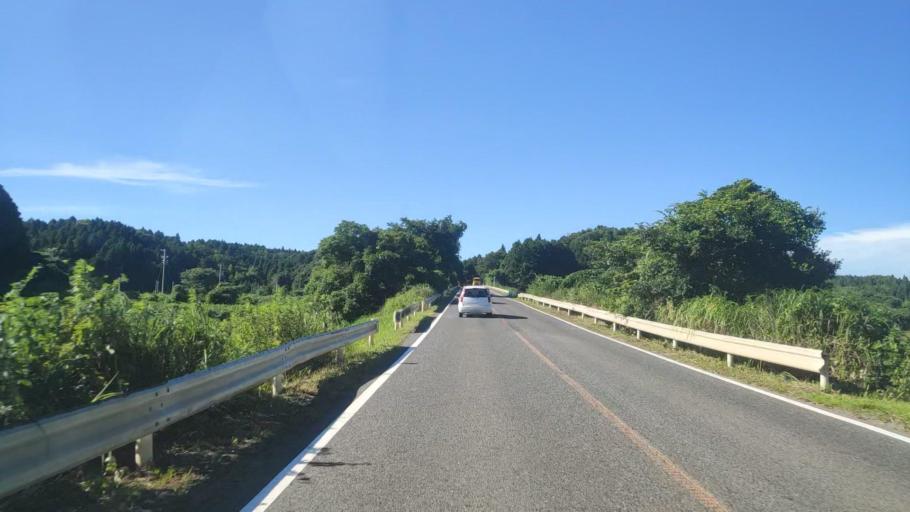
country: JP
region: Mie
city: Ueno-ebisumachi
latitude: 34.8431
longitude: 136.2366
